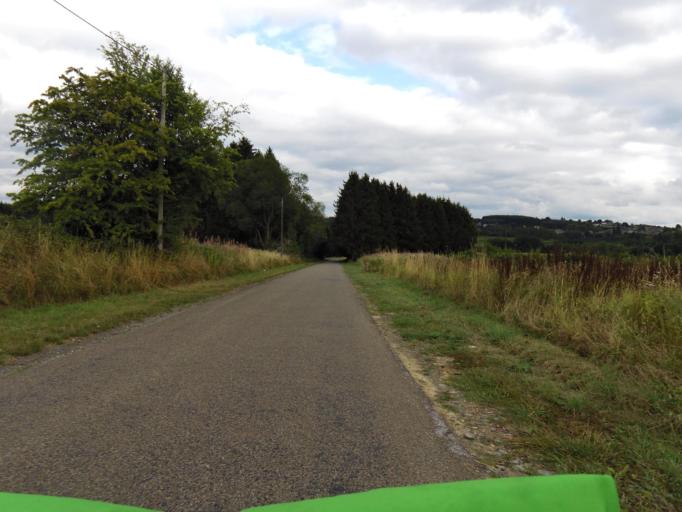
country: BE
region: Wallonia
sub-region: Province de Namur
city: Bievre
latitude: 49.9026
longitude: 4.9992
